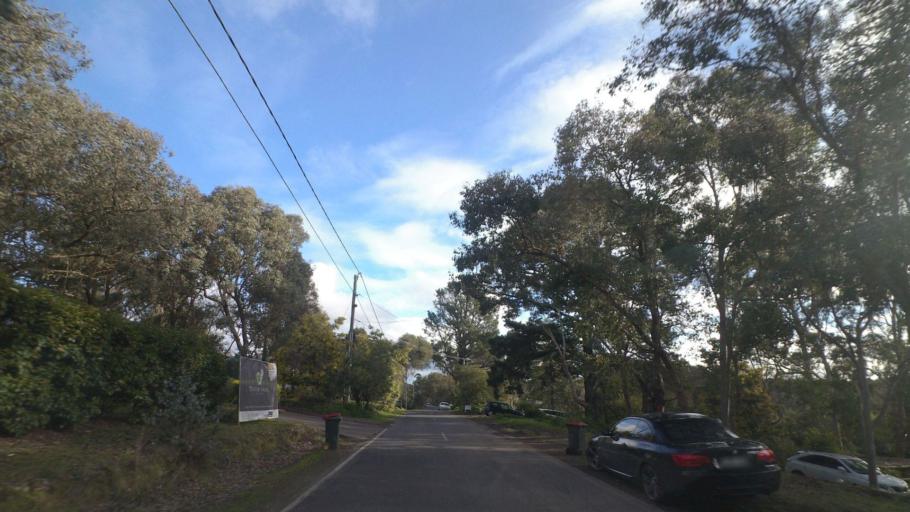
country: AU
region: Victoria
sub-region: Nillumbik
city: North Warrandyte
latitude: -37.7368
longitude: 145.2141
